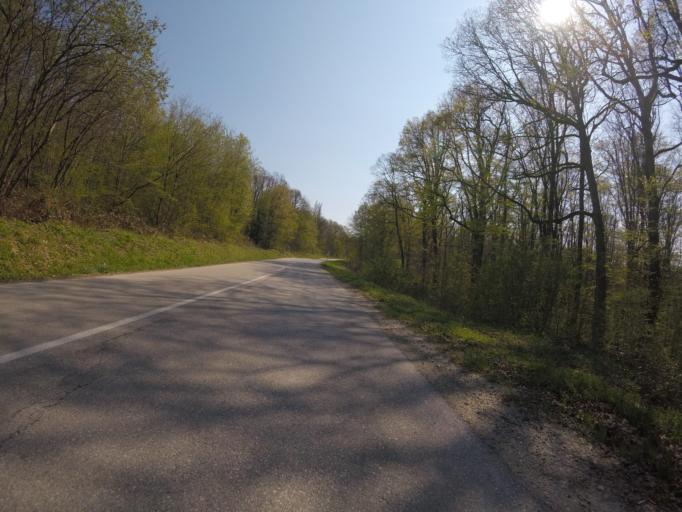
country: HR
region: Zagrebacka
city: Lukavec
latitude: 45.6341
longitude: 15.9624
